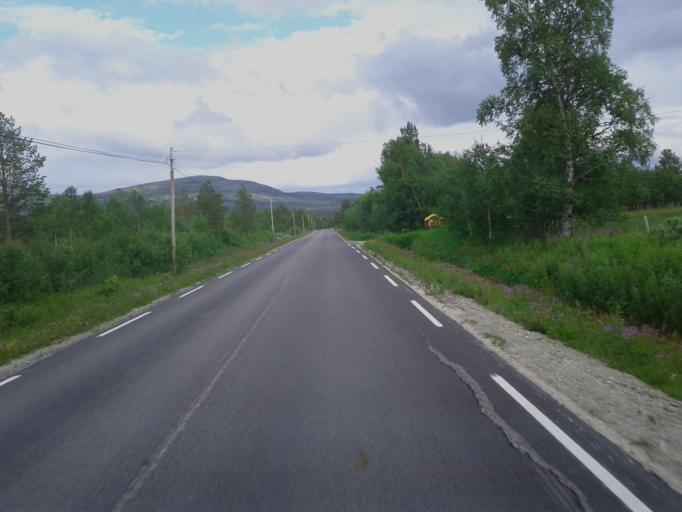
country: NO
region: Sor-Trondelag
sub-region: Roros
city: Roros
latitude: 62.3050
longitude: 11.7066
